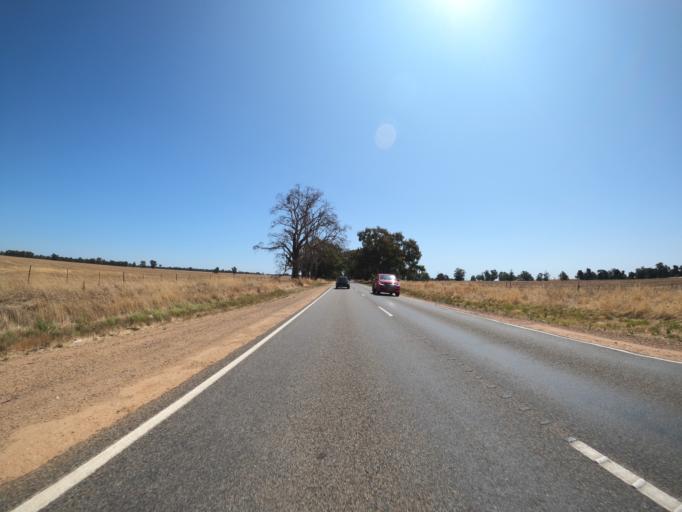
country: AU
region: Victoria
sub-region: Moira
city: Yarrawonga
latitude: -36.0241
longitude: 146.1118
